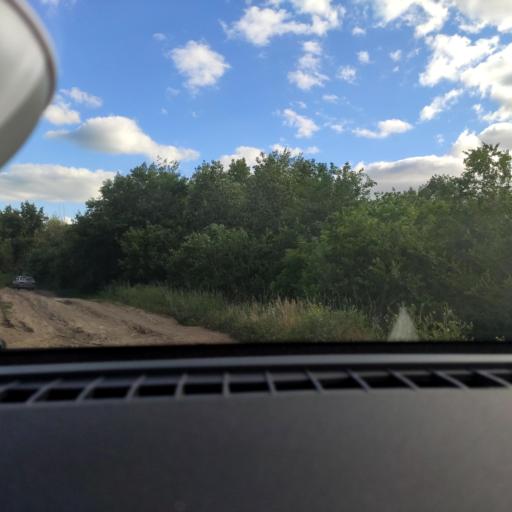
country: RU
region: Samara
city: Samara
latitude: 53.1788
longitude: 50.2370
